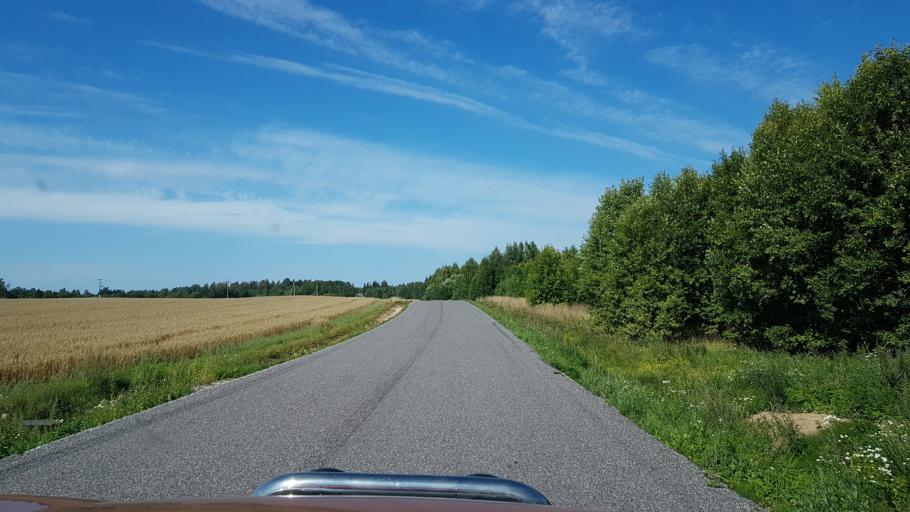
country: EE
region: Tartu
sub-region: Elva linn
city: Elva
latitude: 58.2490
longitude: 26.3410
